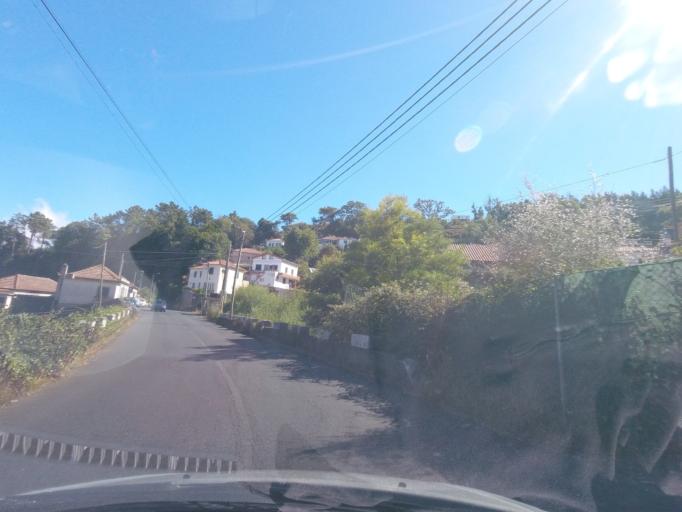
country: PT
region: Madeira
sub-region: Santa Cruz
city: Camacha
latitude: 32.6874
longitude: -16.8526
